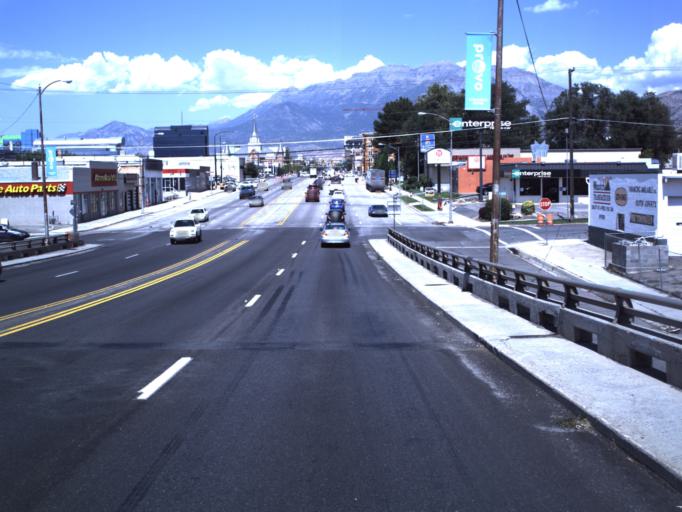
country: US
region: Utah
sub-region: Utah County
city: Provo
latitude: 40.2264
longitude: -111.6587
